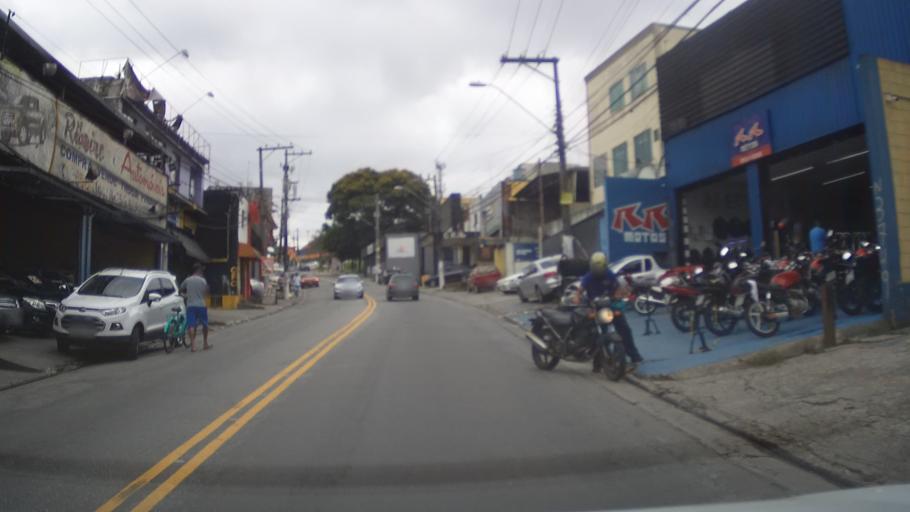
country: BR
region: Sao Paulo
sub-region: Itaquaquecetuba
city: Itaquaquecetuba
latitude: -23.4469
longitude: -46.4081
